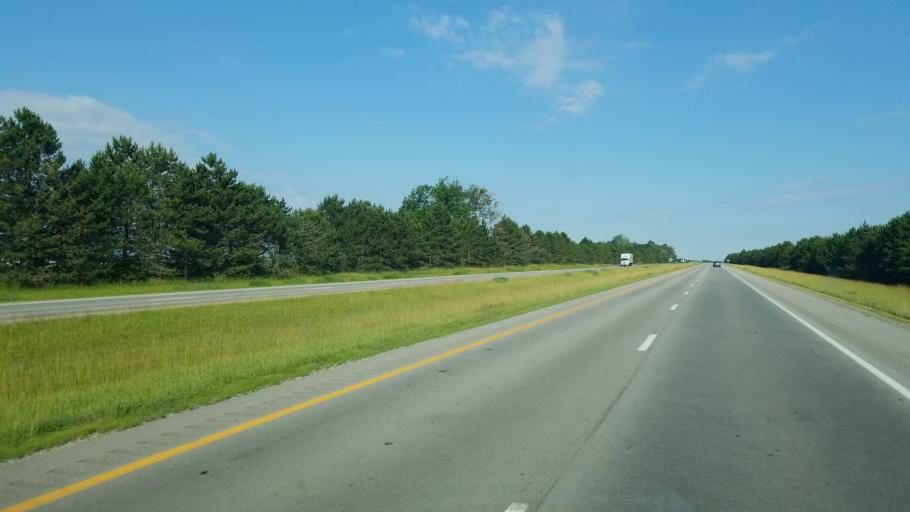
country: US
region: Ohio
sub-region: Wyandot County
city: Carey
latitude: 40.9580
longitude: -83.4508
